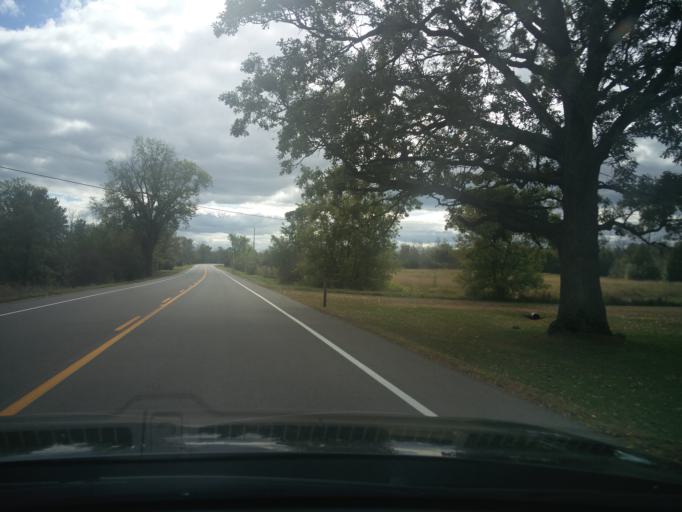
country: CA
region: Ontario
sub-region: Lanark County
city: Smiths Falls
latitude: 45.0157
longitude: -76.0798
